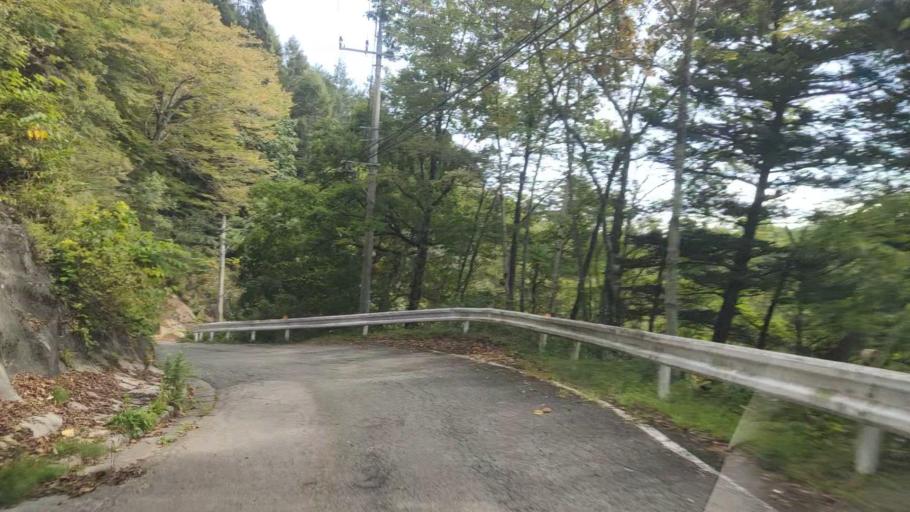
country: JP
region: Gunma
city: Nakanojomachi
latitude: 36.6588
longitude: 138.6278
